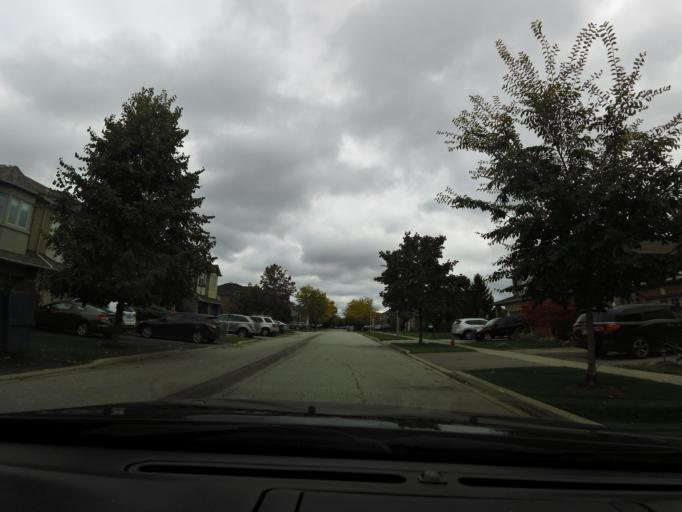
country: CA
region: Ontario
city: Burlington
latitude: 43.3913
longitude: -79.7806
